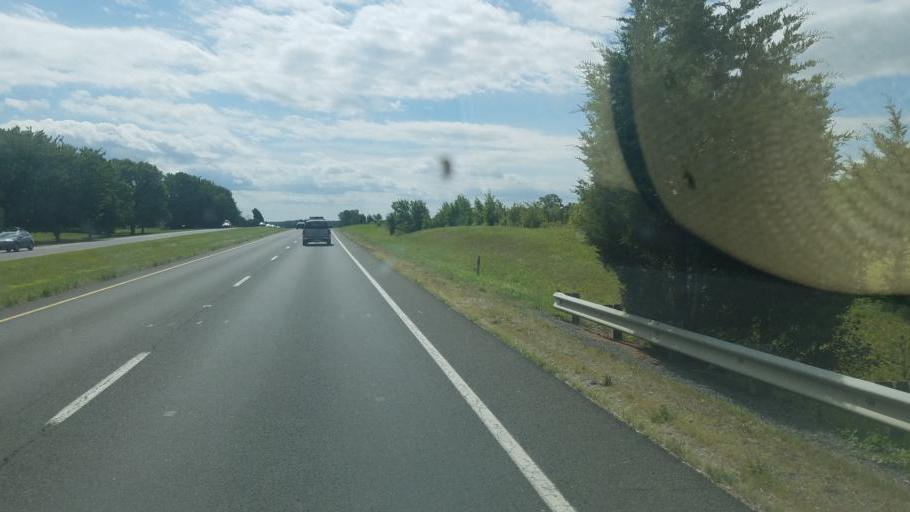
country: US
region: Virginia
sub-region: Fauquier County
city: Bealeton
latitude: 38.4424
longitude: -77.6474
